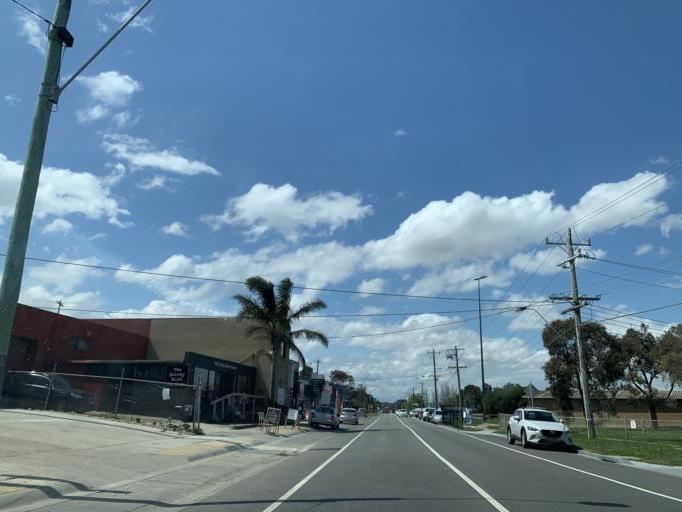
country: AU
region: Victoria
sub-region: Kingston
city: Mordialloc
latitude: -38.0091
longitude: 145.0970
